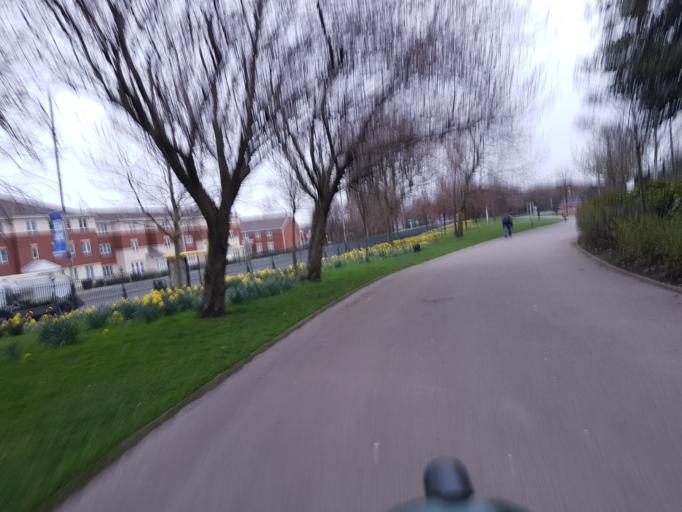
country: GB
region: England
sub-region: Liverpool
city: Liverpool
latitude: 53.4335
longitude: -2.9683
